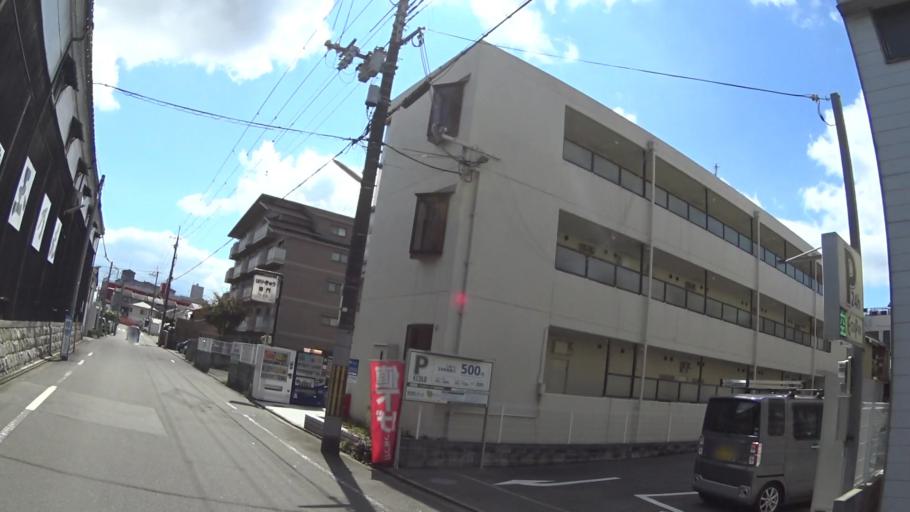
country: JP
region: Kyoto
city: Muko
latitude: 34.9384
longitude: 135.7577
